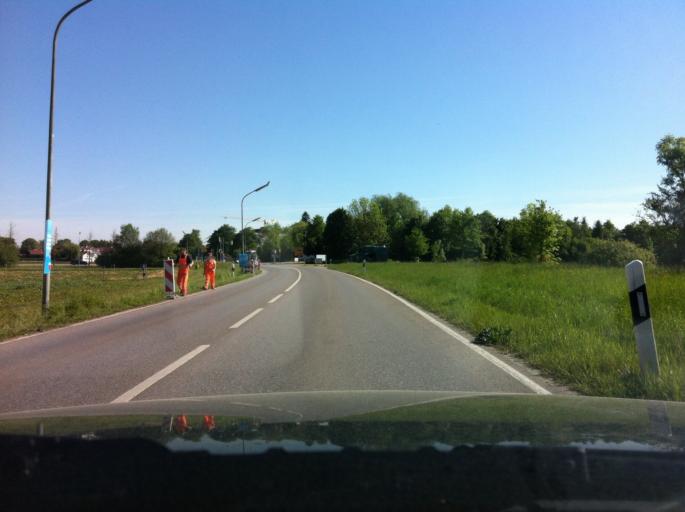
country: DE
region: Bavaria
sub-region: Upper Bavaria
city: Taufkirchen
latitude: 48.0523
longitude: 11.6180
